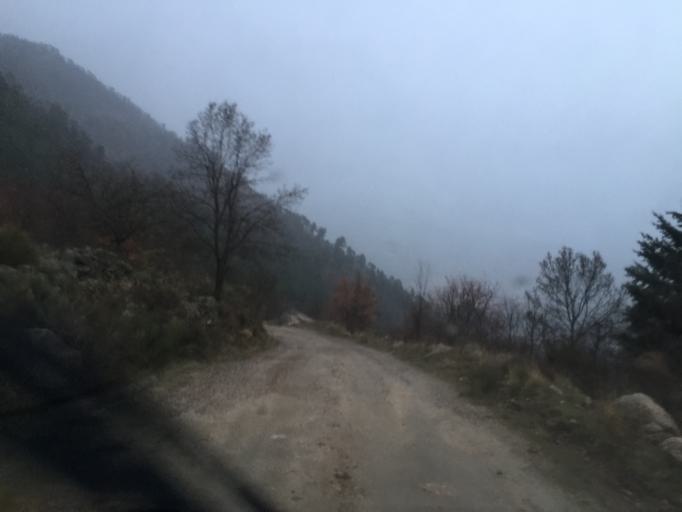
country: PT
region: Guarda
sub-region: Manteigas
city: Manteigas
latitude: 40.3807
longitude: -7.5480
